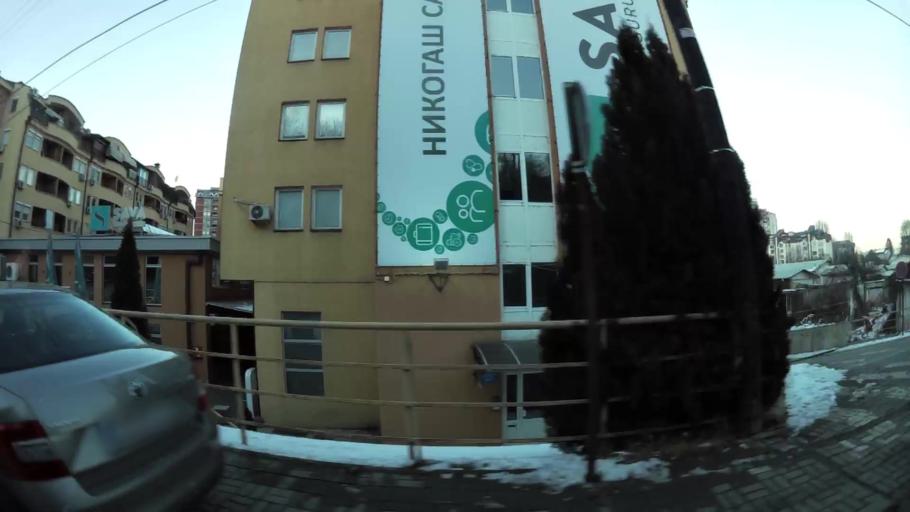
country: MK
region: Karpos
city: Skopje
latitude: 41.9919
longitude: 21.4120
